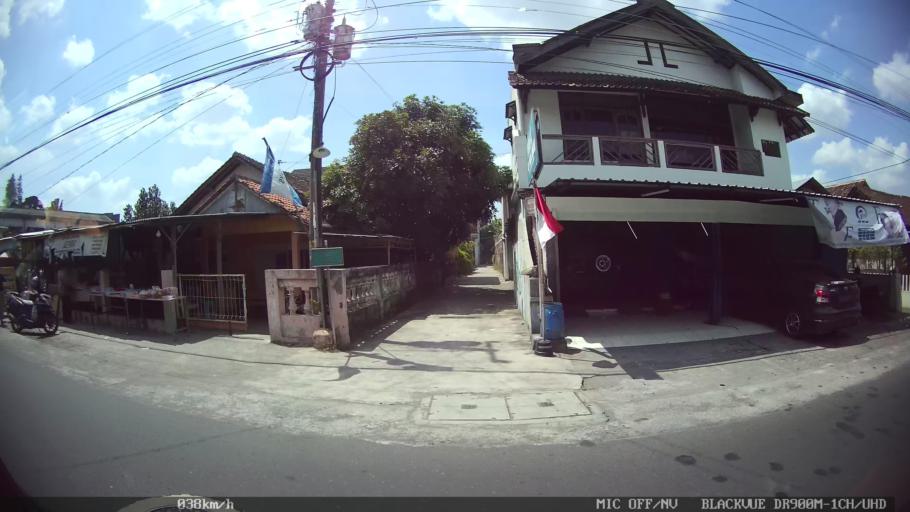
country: ID
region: Daerah Istimewa Yogyakarta
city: Kasihan
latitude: -7.8190
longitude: 110.3481
